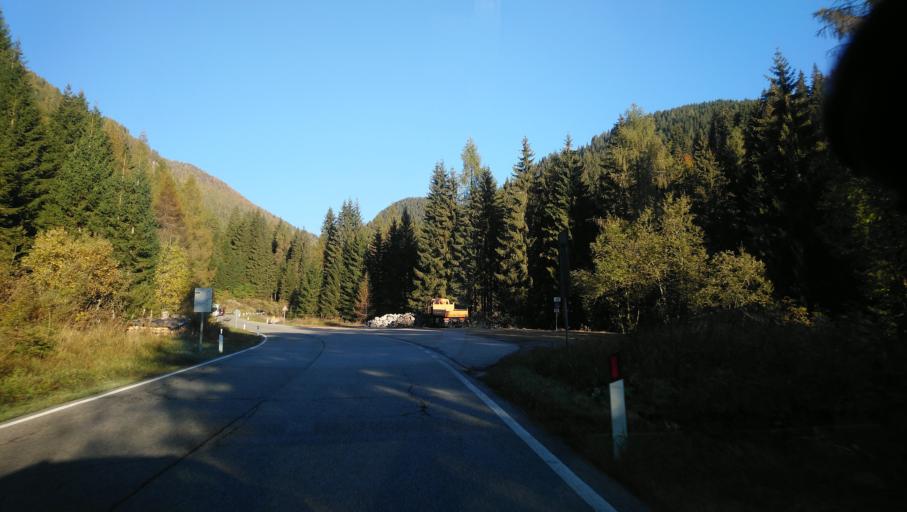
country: IT
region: Veneto
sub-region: Provincia di Belluno
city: Falcade Alto
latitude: 46.3600
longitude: 11.8463
